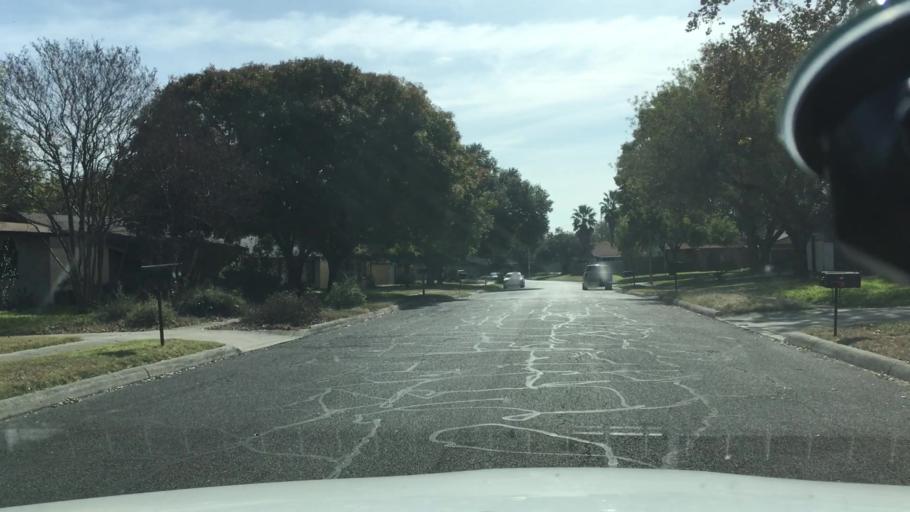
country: US
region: Texas
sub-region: Bexar County
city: Windcrest
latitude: 29.5739
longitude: -98.4166
